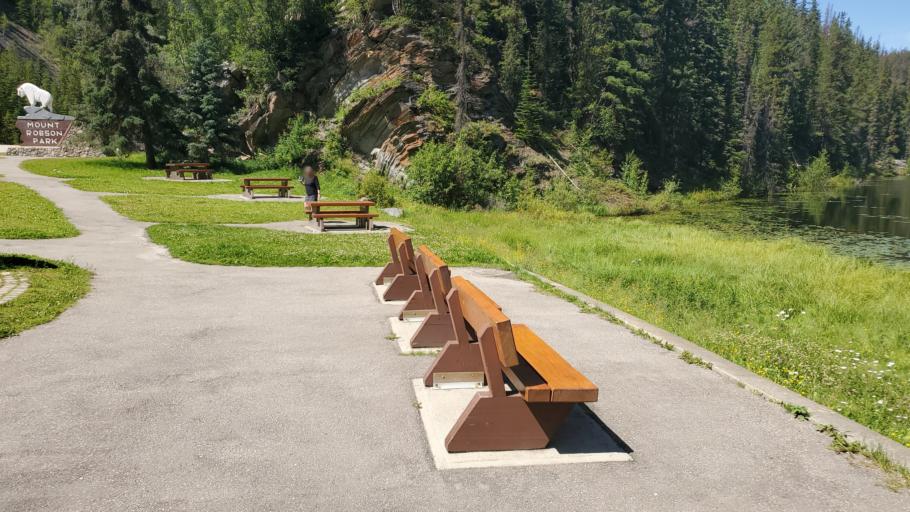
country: CA
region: Alberta
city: Jasper Park Lodge
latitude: 52.8822
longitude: -118.4511
